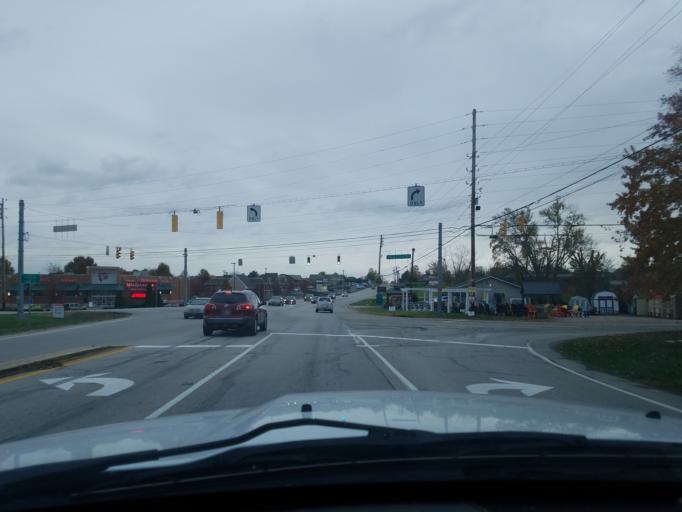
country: US
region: Indiana
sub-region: Clark County
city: Sellersburg
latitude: 38.3685
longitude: -85.7763
